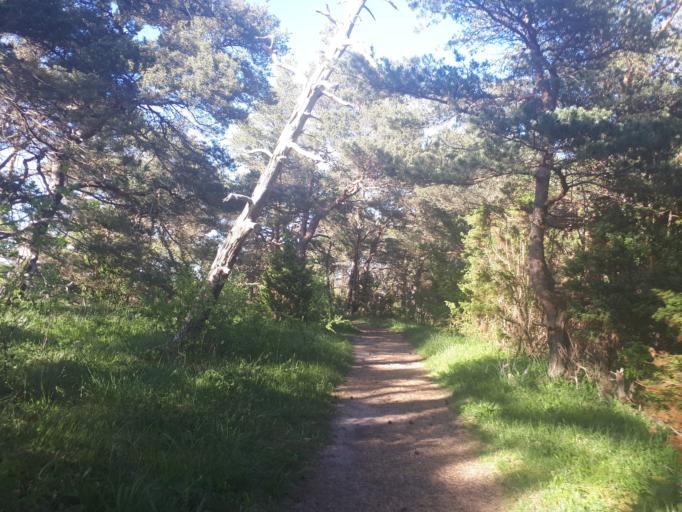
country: SE
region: Gotland
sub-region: Gotland
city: Vibble
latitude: 57.6142
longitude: 18.2515
